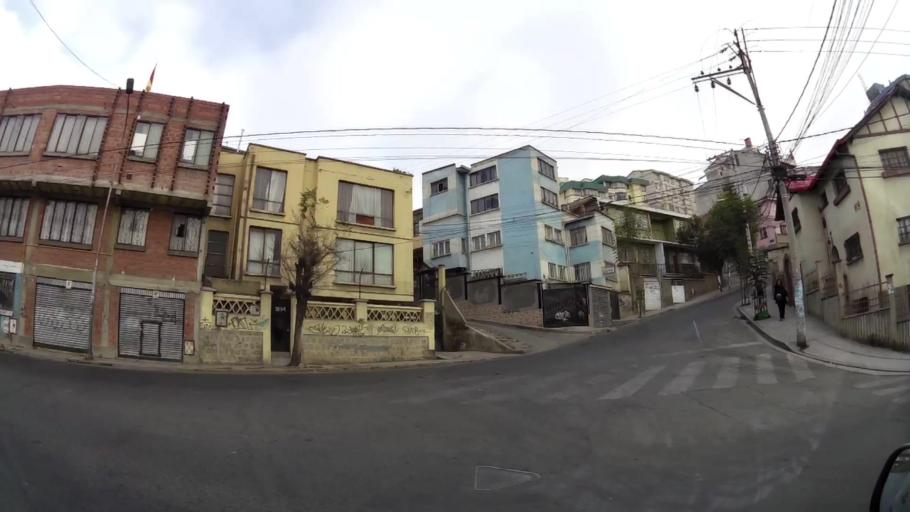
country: BO
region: La Paz
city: La Paz
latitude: -16.5018
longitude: -68.1241
